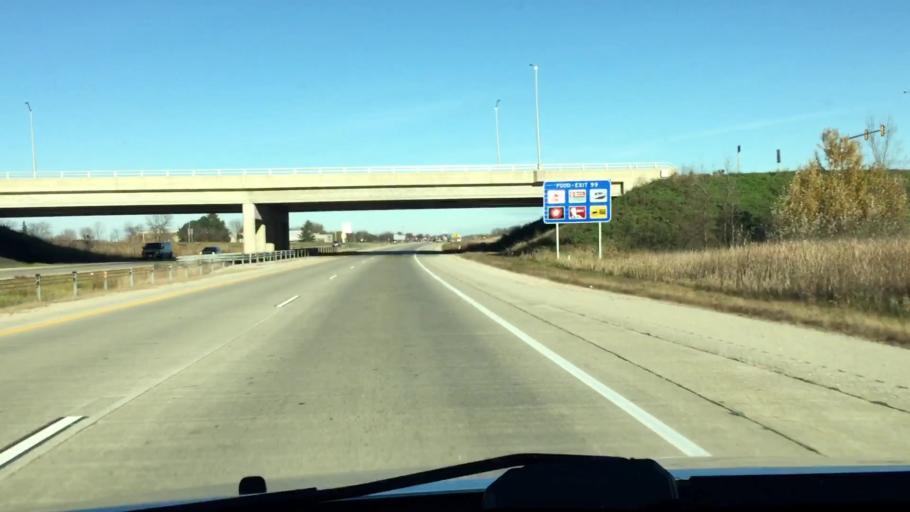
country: US
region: Wisconsin
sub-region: Fond du Lac County
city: Fond du Lac
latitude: 43.7580
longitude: -88.4740
